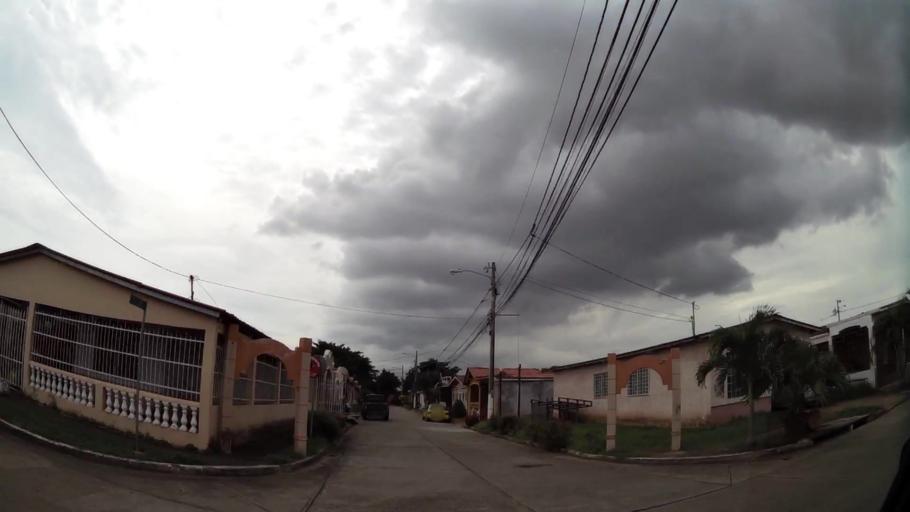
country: PA
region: Panama
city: Tocumen
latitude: 9.0469
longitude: -79.4083
